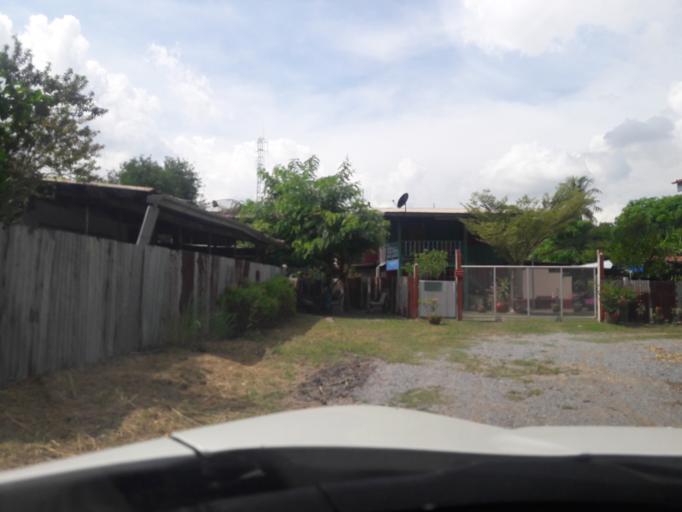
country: TH
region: Lop Buri
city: Ban Mi
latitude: 15.0304
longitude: 100.5395
